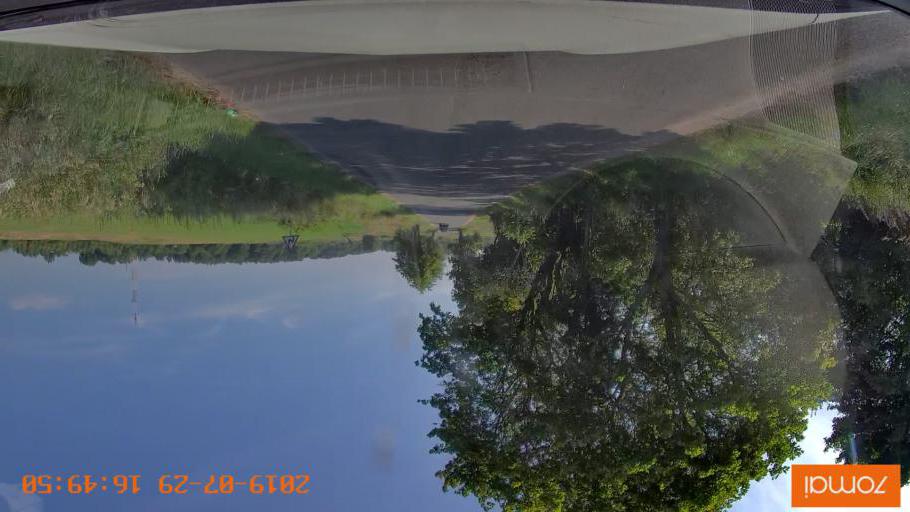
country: RU
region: Kaliningrad
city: Primorsk
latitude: 54.7978
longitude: 20.0609
